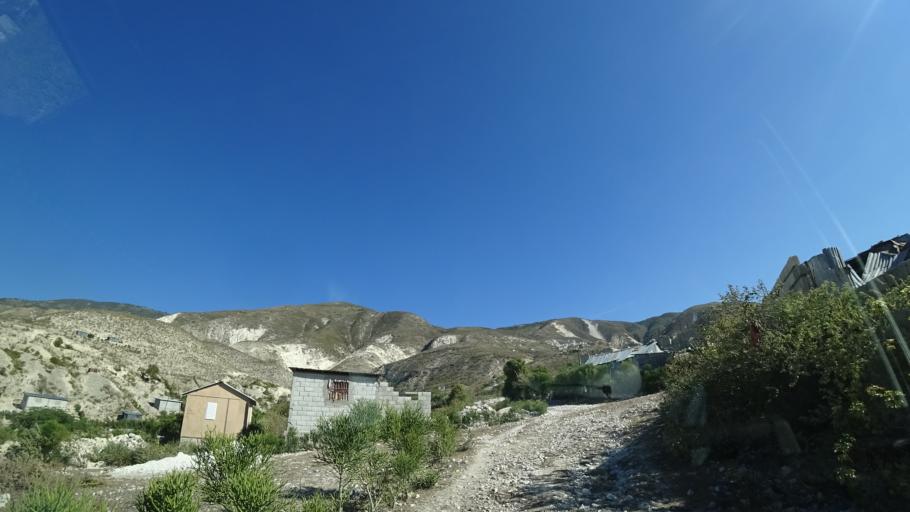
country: HT
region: Ouest
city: Croix des Bouquets
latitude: 18.6769
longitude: -72.2395
